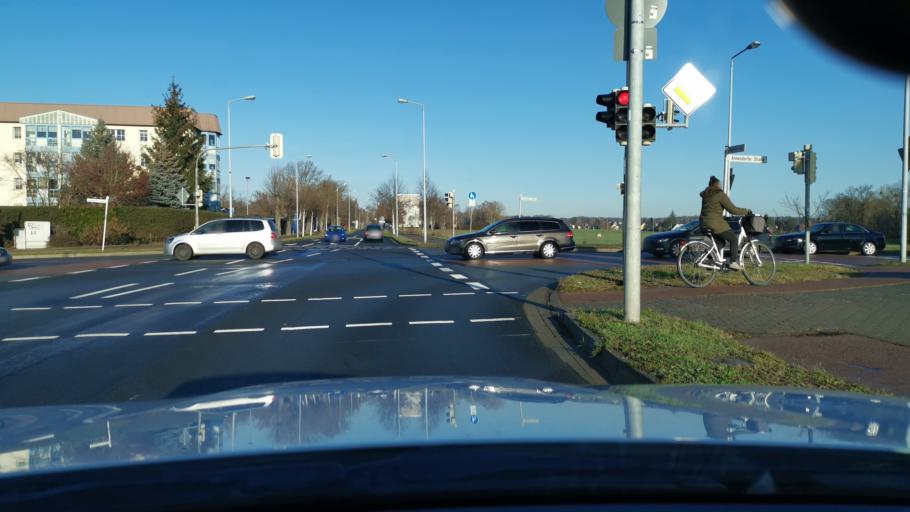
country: DE
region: Saxony-Anhalt
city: Wittenburg
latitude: 51.8820
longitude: 12.6520
